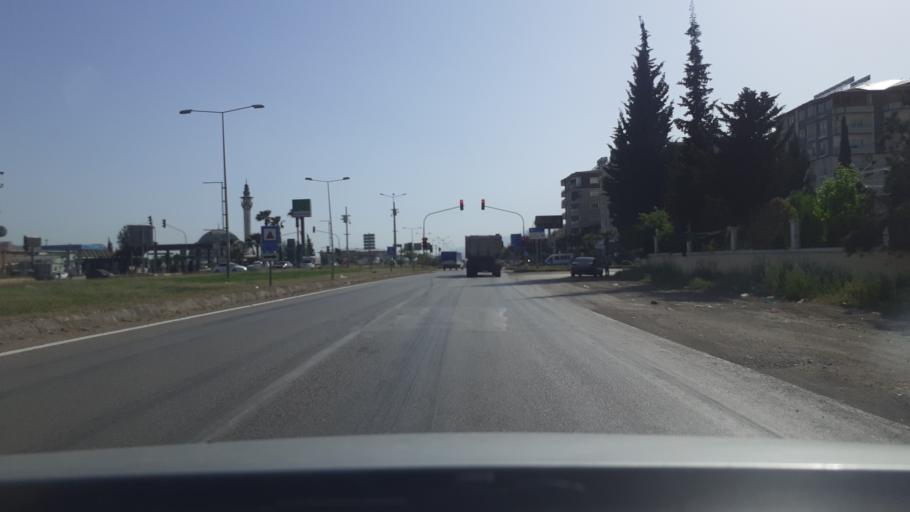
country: TR
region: Hatay
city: Kirikhan
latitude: 36.4880
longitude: 36.3667
